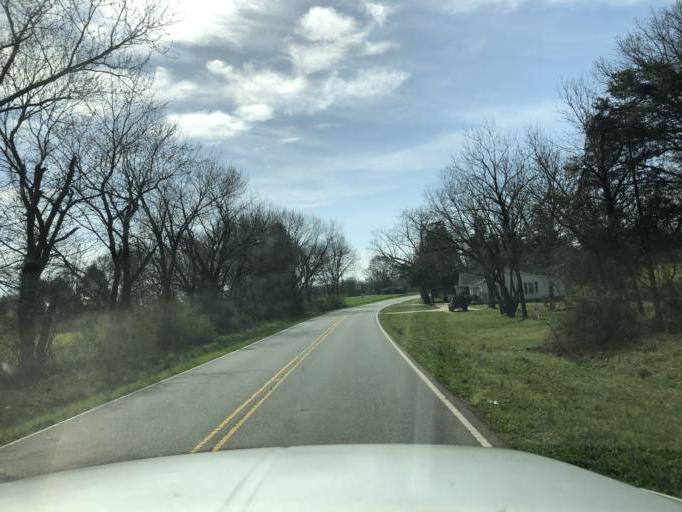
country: US
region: North Carolina
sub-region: Cleveland County
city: Shelby
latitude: 35.3982
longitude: -81.6271
